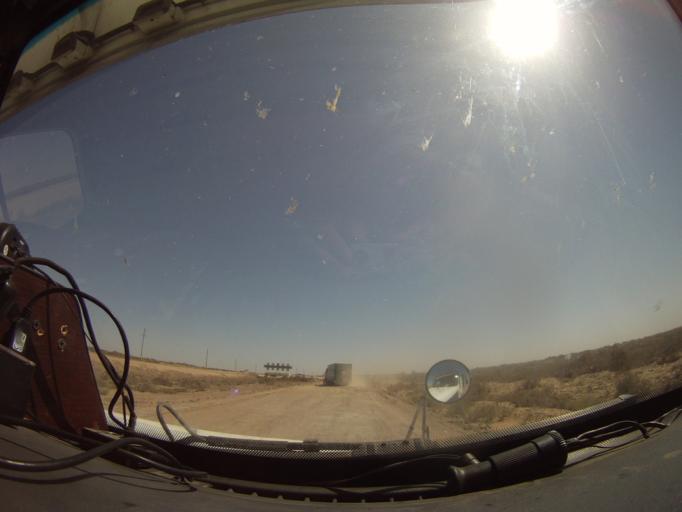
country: KZ
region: Qyzylorda
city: Dzhalagash
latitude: 44.8915
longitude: 64.7379
